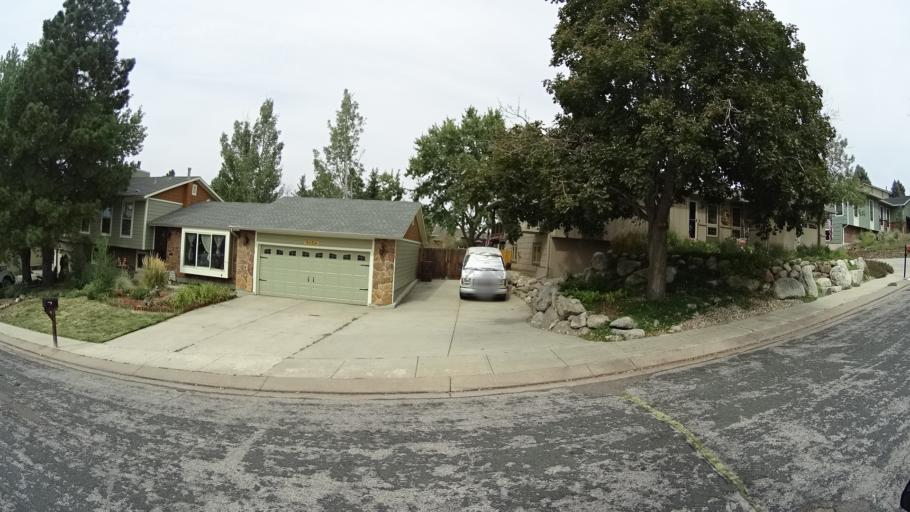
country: US
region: Colorado
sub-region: El Paso County
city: Cimarron Hills
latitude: 38.8969
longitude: -104.7320
